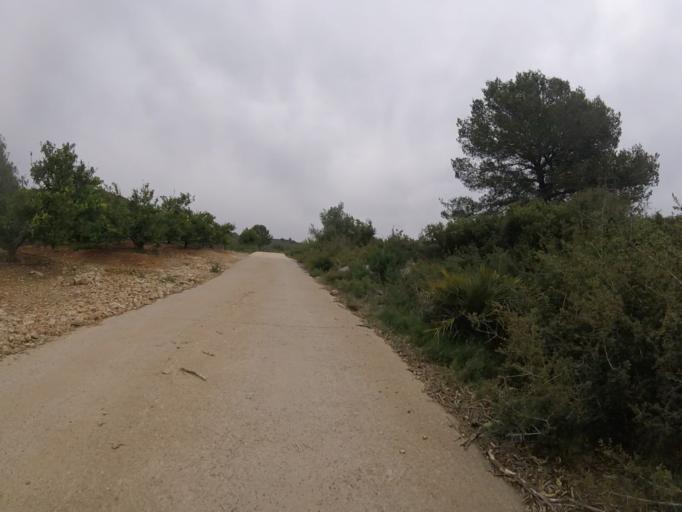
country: ES
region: Valencia
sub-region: Provincia de Castello
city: Alcala de Xivert
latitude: 40.2939
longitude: 0.2548
